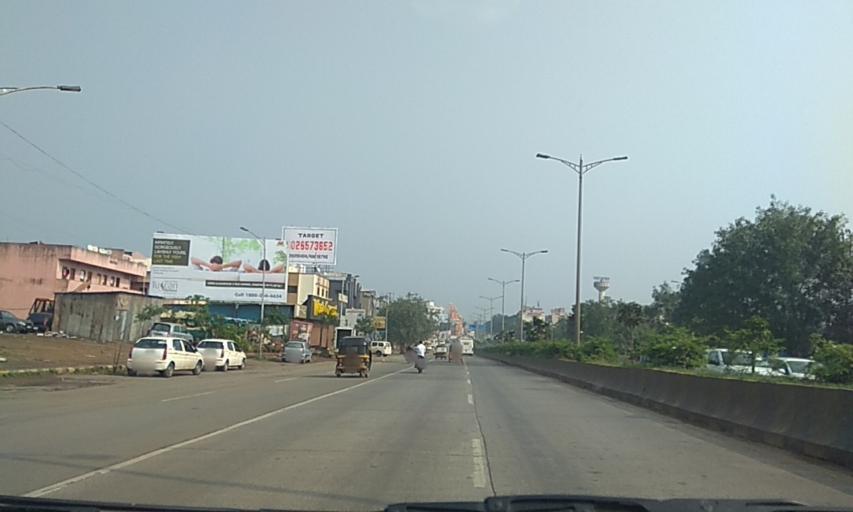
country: IN
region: Maharashtra
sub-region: Pune Division
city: Lohogaon
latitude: 18.5551
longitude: 73.9376
